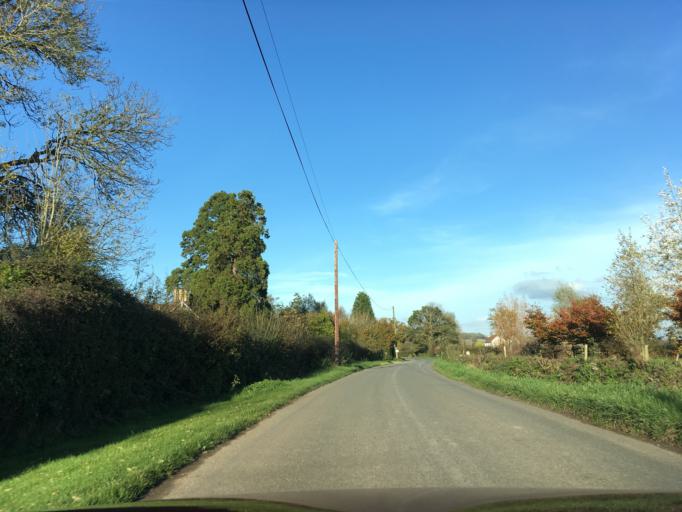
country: GB
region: England
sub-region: South Gloucestershire
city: Hill
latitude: 51.6342
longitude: -2.5102
